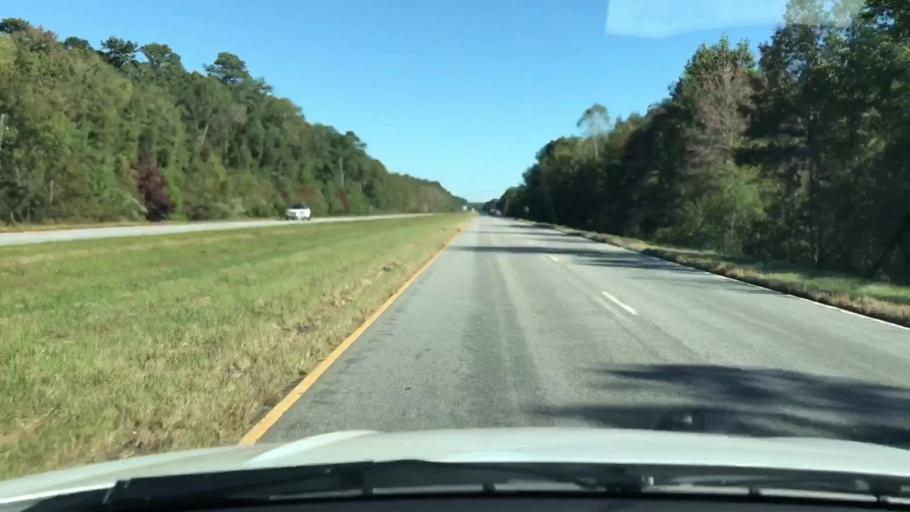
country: US
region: South Carolina
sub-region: Charleston County
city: Ravenel
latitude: 32.7618
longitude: -80.4173
